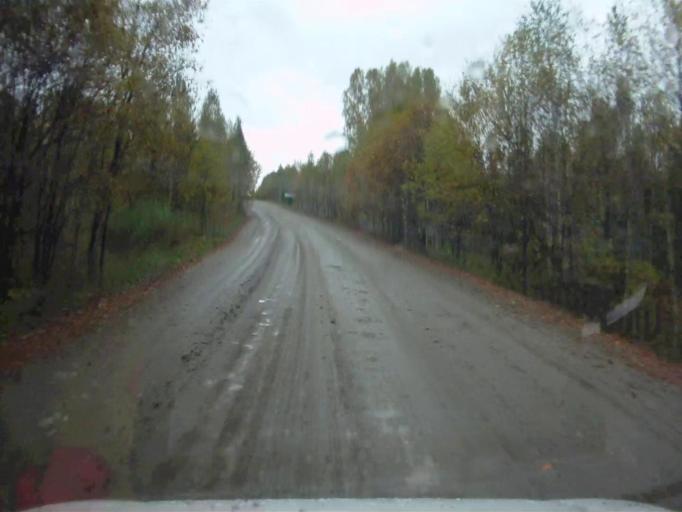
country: RU
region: Chelyabinsk
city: Kyshtym
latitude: 55.8457
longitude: 60.4855
